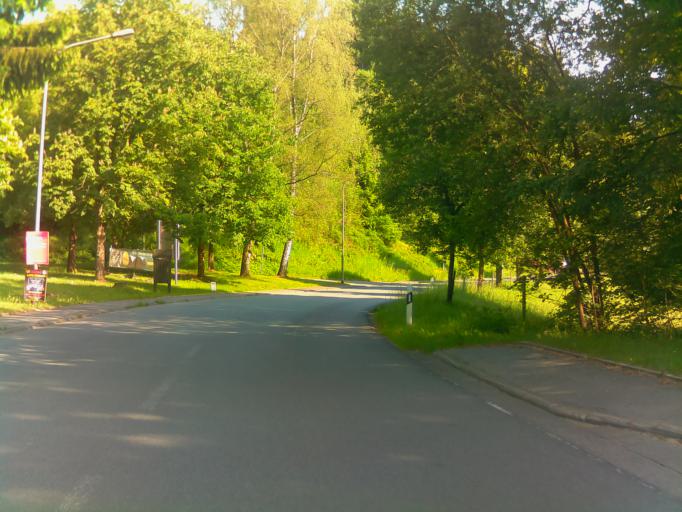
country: DE
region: Hesse
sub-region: Regierungsbezirk Darmstadt
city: Furth
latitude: 49.6323
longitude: 8.8380
